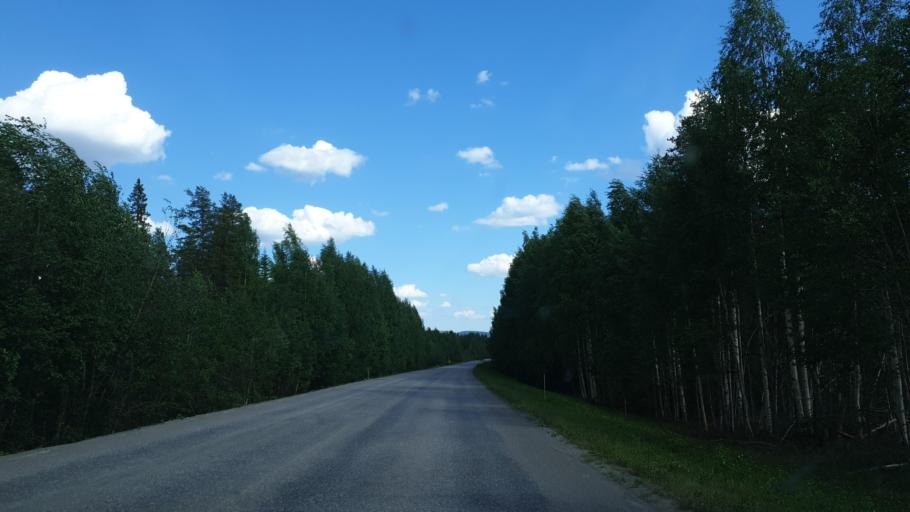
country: SE
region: Norrbotten
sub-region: Alvsbyns Kommun
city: AElvsbyn
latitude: 65.8435
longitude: 20.4933
